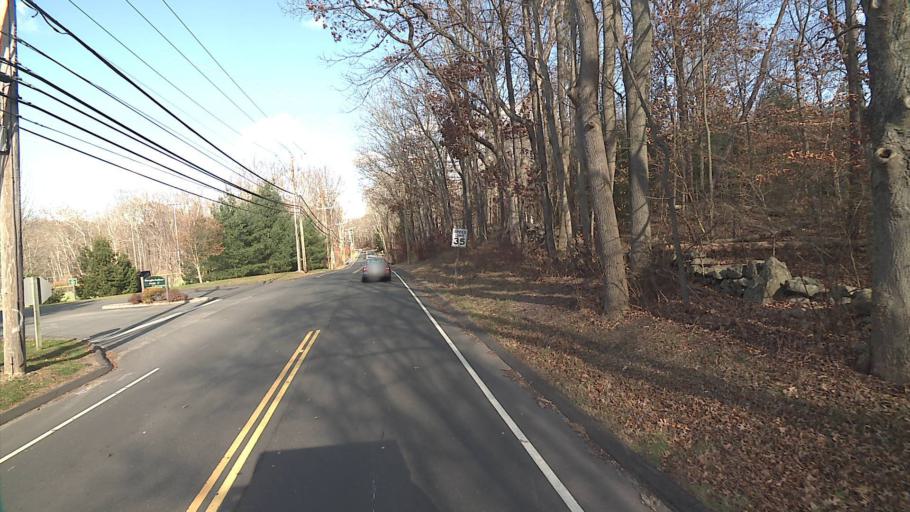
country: US
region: Connecticut
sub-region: Fairfield County
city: Wilton
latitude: 41.2132
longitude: -73.3864
